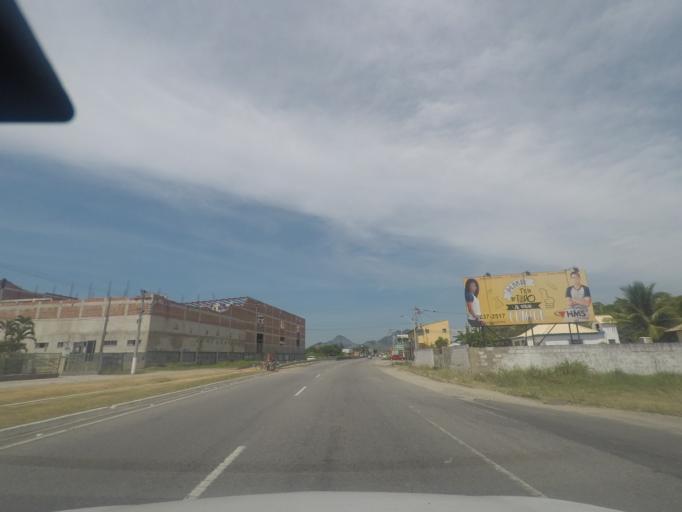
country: BR
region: Rio de Janeiro
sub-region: Marica
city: Marica
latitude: -22.9077
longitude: -42.8273
